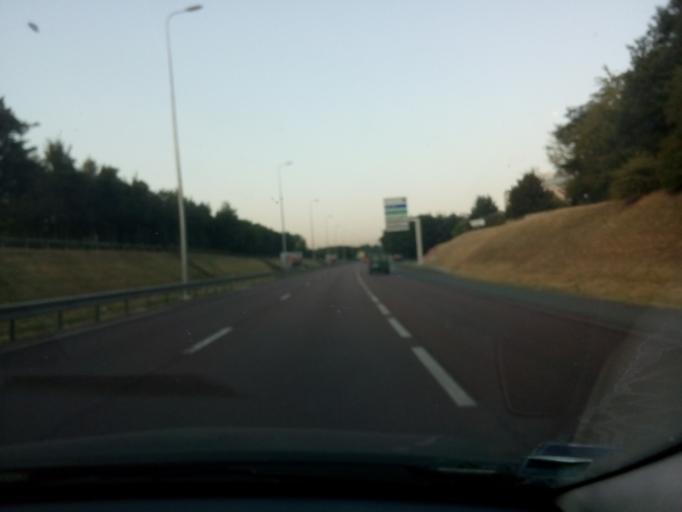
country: FR
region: Ile-de-France
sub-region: Departement du Val-d'Oise
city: Roissy-en-France
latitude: 48.9986
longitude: 2.5189
